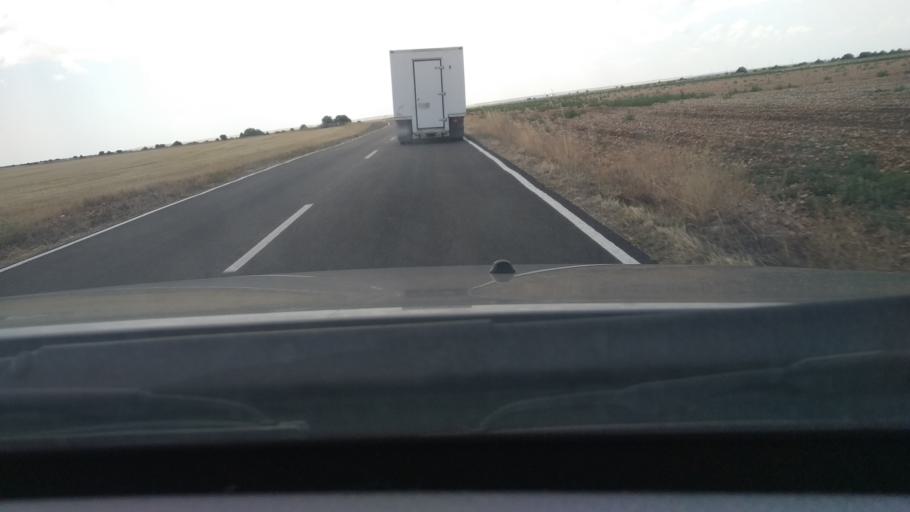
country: ES
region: Castille and Leon
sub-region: Provincia de Burgos
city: Iglesiarrubia
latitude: 41.9514
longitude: -3.8347
